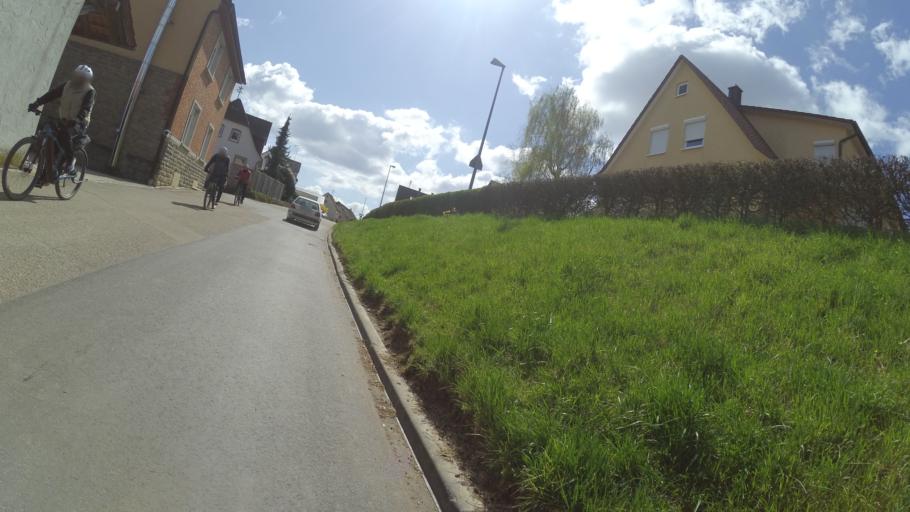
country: DE
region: Baden-Wuerttemberg
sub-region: Regierungsbezirk Stuttgart
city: Oedheim
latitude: 49.2515
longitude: 9.2871
